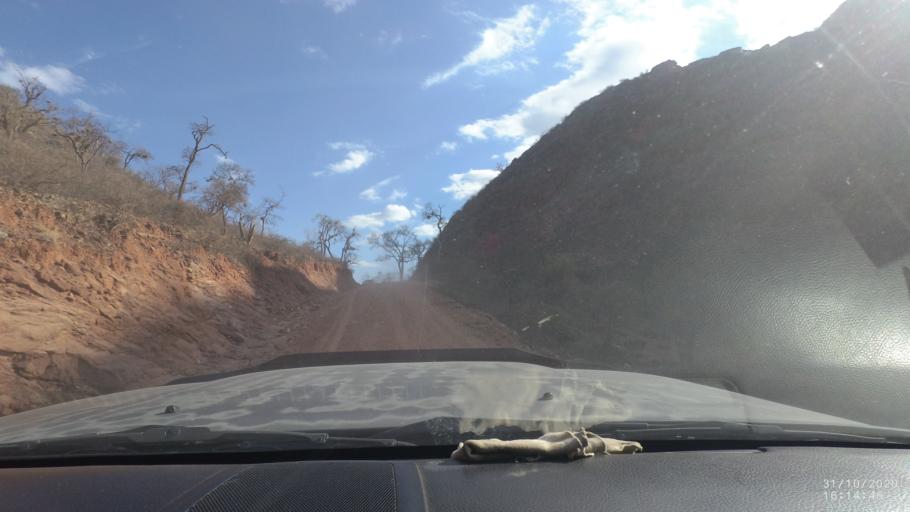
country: BO
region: Chuquisaca
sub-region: Provincia Zudanez
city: Mojocoya
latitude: -18.3852
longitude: -64.6145
